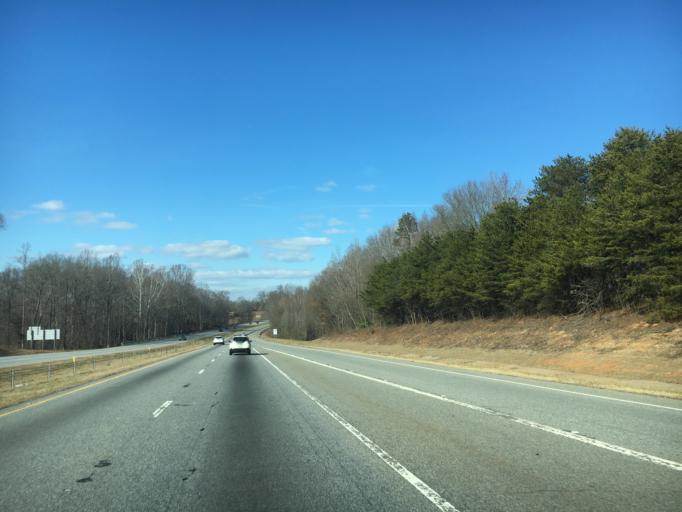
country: US
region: South Carolina
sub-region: Spartanburg County
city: Southern Shops
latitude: 35.0118
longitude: -82.0301
